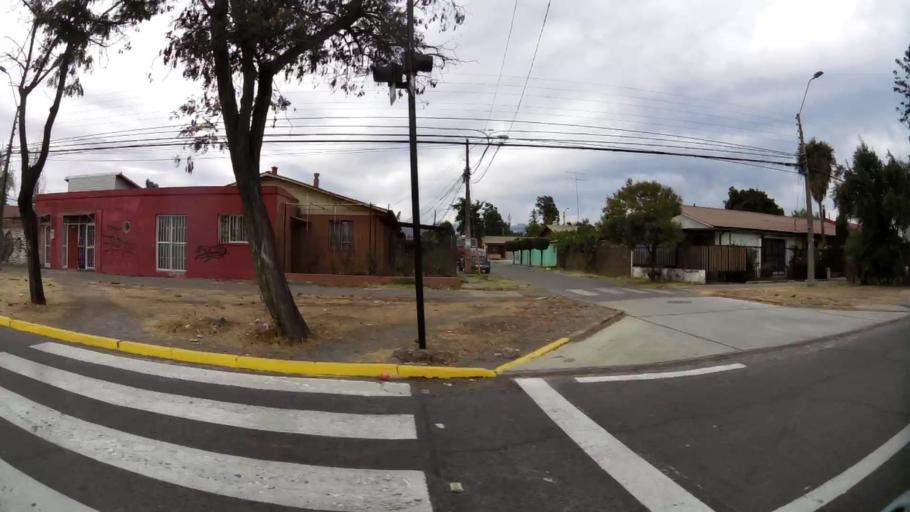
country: CL
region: O'Higgins
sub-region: Provincia de Cachapoal
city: Rancagua
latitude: -34.1529
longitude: -70.7430
